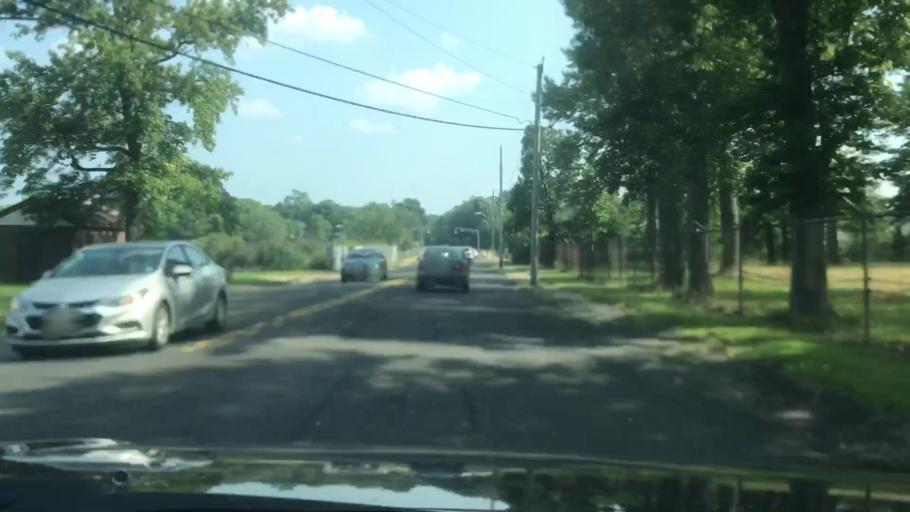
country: US
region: New Jersey
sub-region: Monmouth County
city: Oceanport
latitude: 40.3157
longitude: -74.0324
